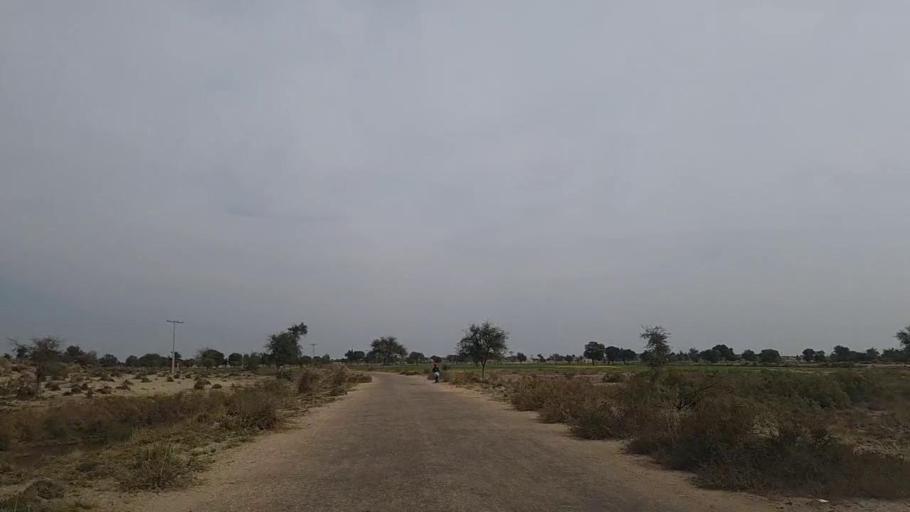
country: PK
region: Sindh
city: Jam Sahib
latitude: 26.3997
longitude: 68.5127
